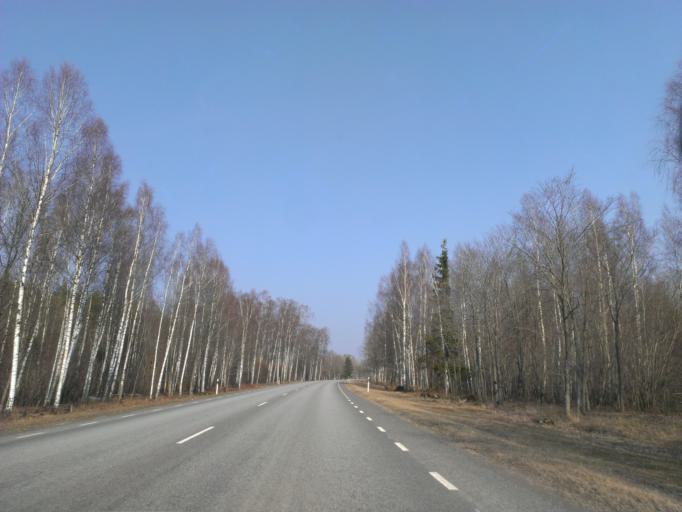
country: EE
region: Saare
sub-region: Orissaare vald
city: Orissaare
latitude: 58.4853
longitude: 22.8398
